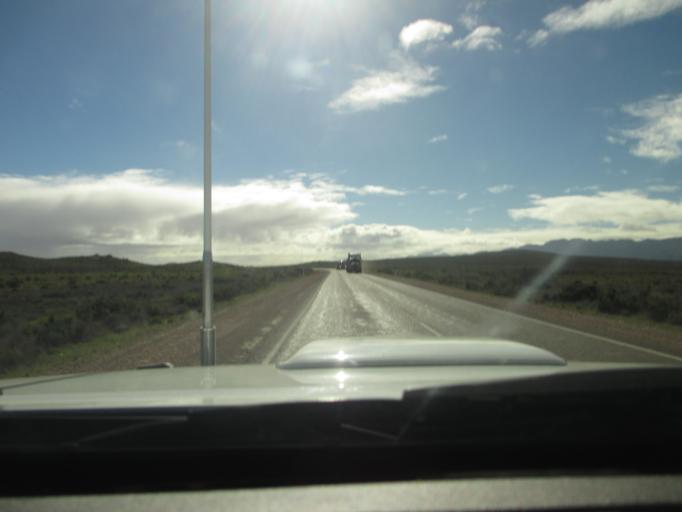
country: AU
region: South Australia
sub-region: Flinders Ranges
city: Quorn
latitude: -31.7517
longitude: 138.3355
